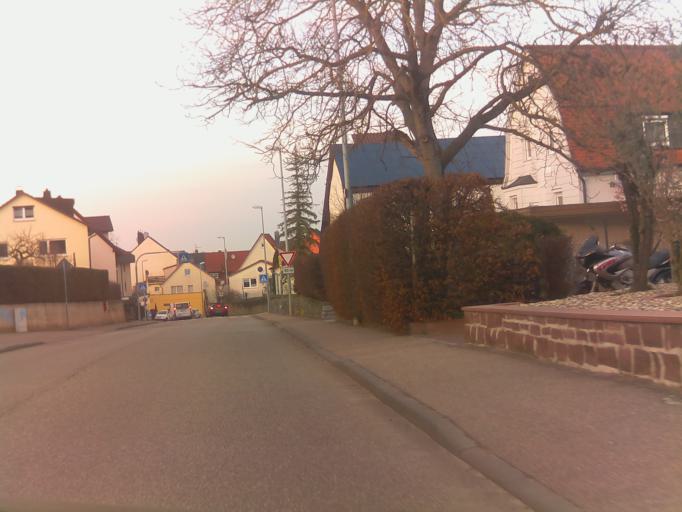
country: DE
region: Baden-Wuerttemberg
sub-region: Regierungsbezirk Stuttgart
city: Hemmingen
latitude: 48.8630
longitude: 9.0304
